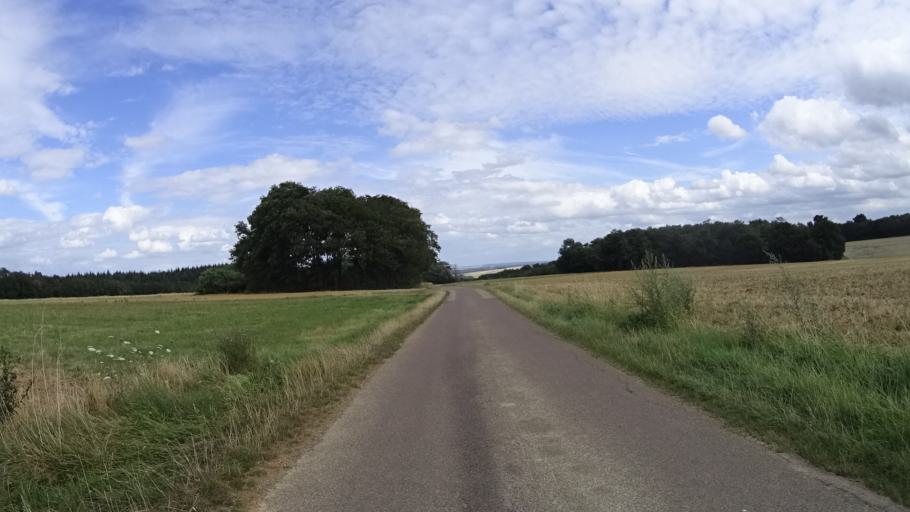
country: FR
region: Bourgogne
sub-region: Departement de l'Yonne
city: Saint-Julien-du-Sault
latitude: 47.9876
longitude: 3.2580
